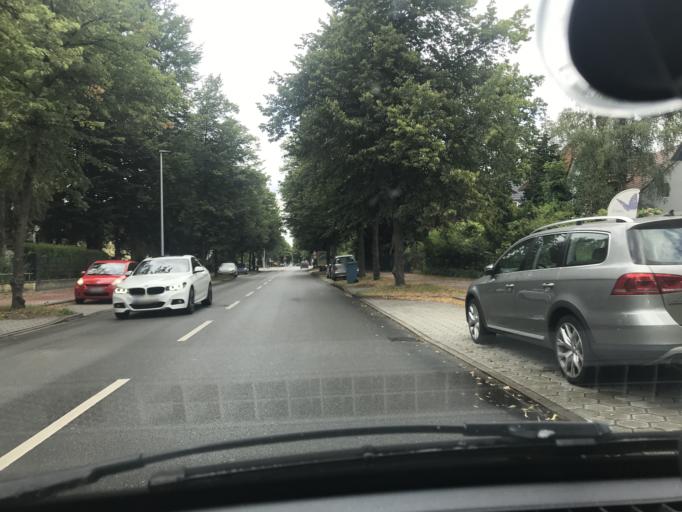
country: DE
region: Schleswig-Holstein
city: Ahrensburg
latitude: 53.6659
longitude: 10.2475
